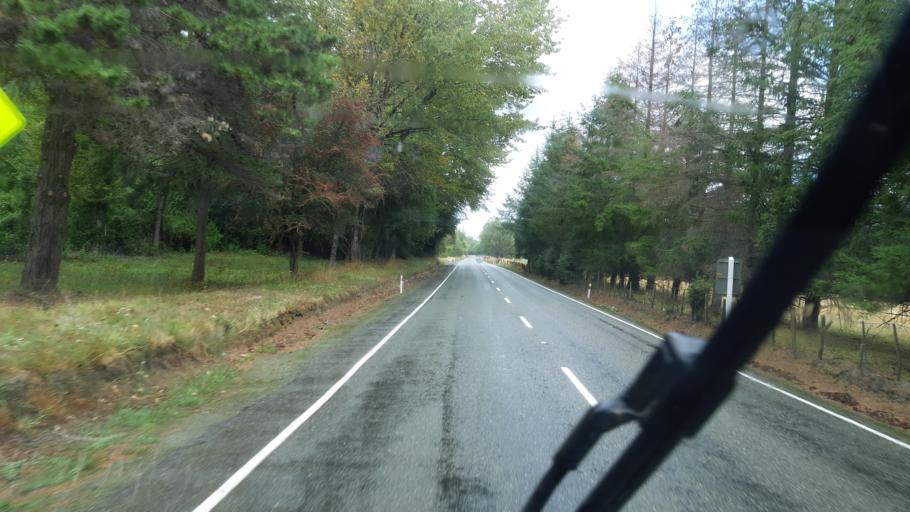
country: NZ
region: Tasman
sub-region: Tasman District
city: Wakefield
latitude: -41.4607
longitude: 172.8385
